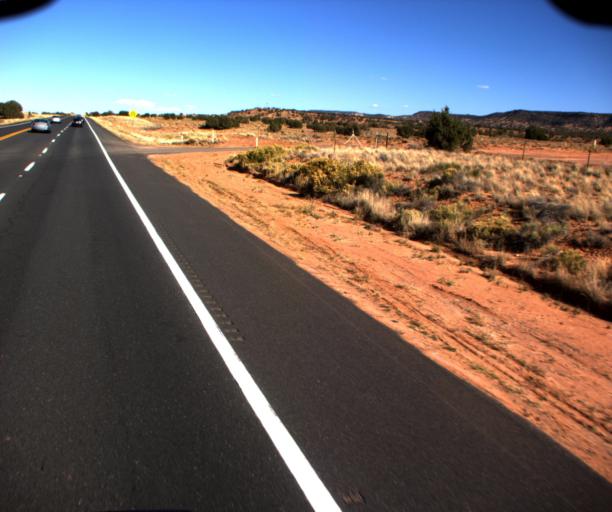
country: US
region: Arizona
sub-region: Coconino County
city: Kaibito
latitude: 36.4034
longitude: -110.8474
